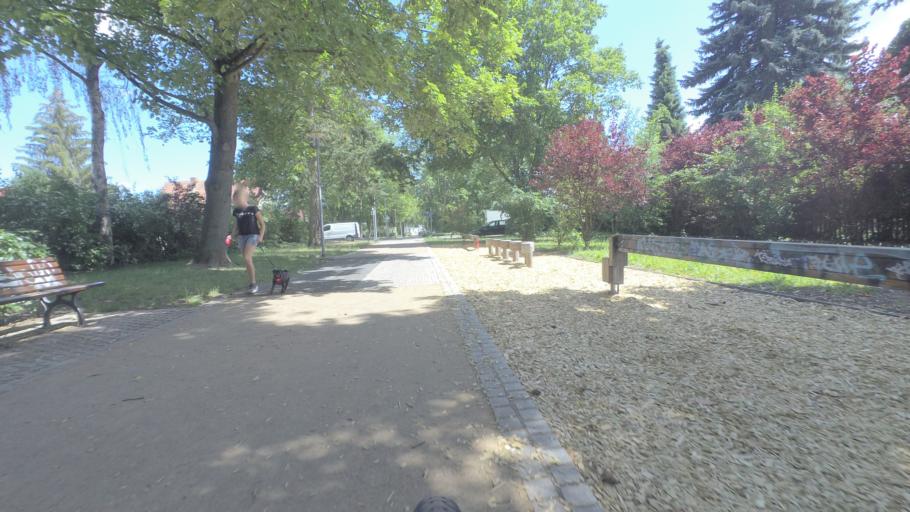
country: DE
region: Brandenburg
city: Rangsdorf
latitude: 52.3345
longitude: 13.4003
